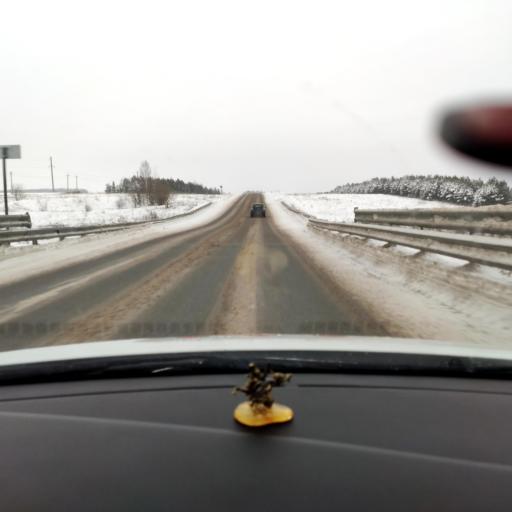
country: RU
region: Tatarstan
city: Vysokaya Gora
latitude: 56.0183
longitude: 49.2691
